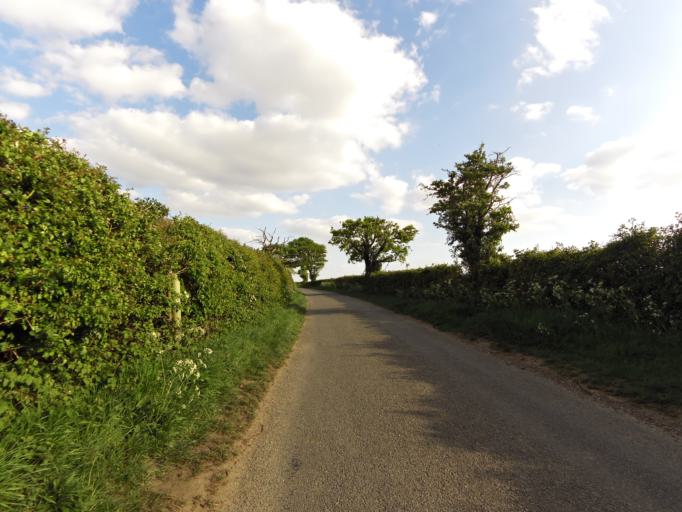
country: GB
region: England
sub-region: Suffolk
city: Halesworth
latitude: 52.4021
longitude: 1.5083
